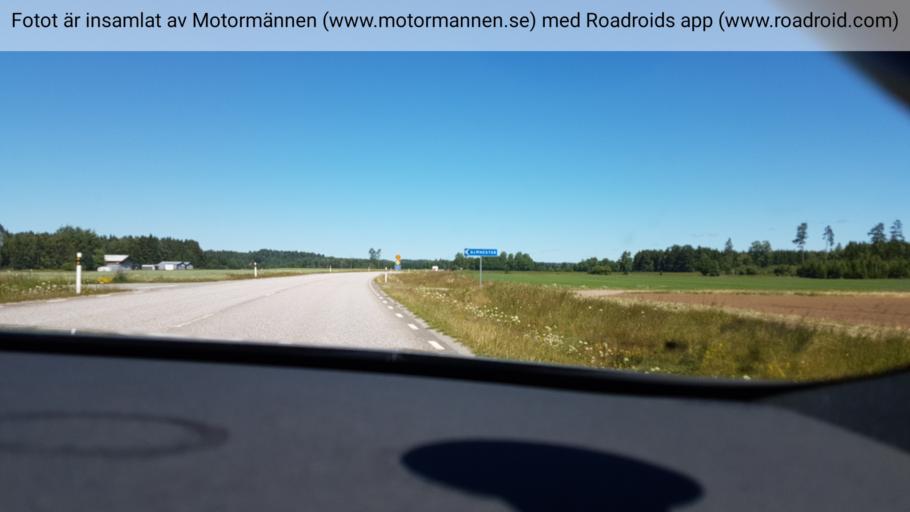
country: SE
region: Vaestra Goetaland
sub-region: Ulricehamns Kommun
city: Ulricehamn
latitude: 57.8696
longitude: 13.4312
